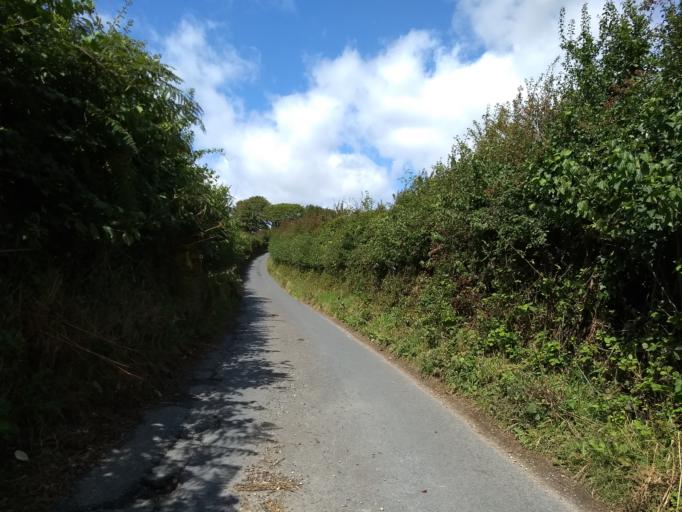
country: GB
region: England
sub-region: Isle of Wight
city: Newport
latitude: 50.6854
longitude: -1.3028
